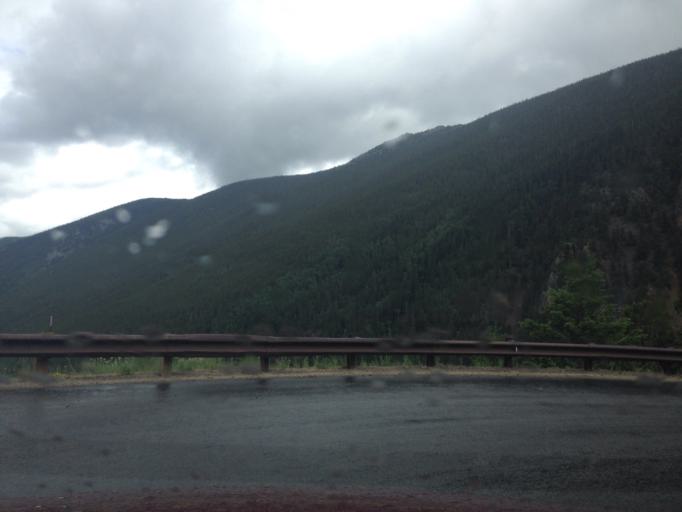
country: US
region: Colorado
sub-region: Clear Creek County
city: Georgetown
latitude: 39.6792
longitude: -105.7029
